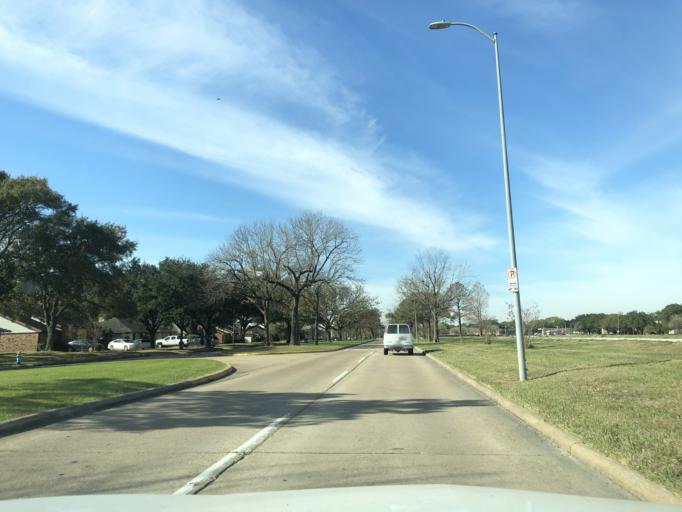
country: US
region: Texas
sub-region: Harris County
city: Bellaire
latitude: 29.6759
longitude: -95.4899
